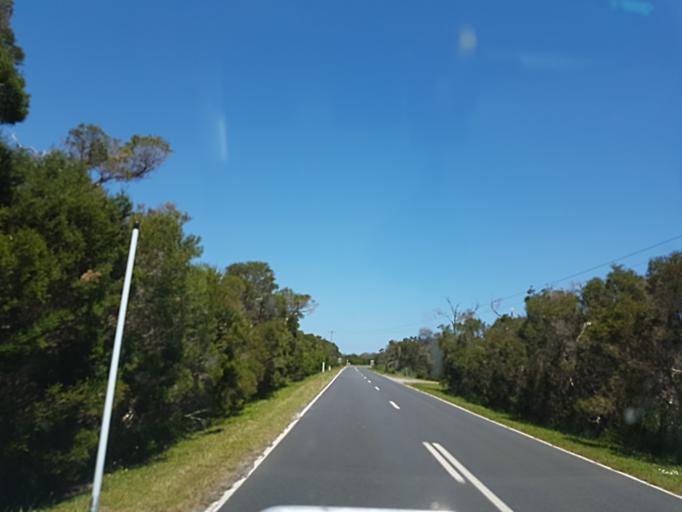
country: AU
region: Victoria
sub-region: Bass Coast
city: North Wonthaggi
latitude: -38.6971
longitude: 145.8784
